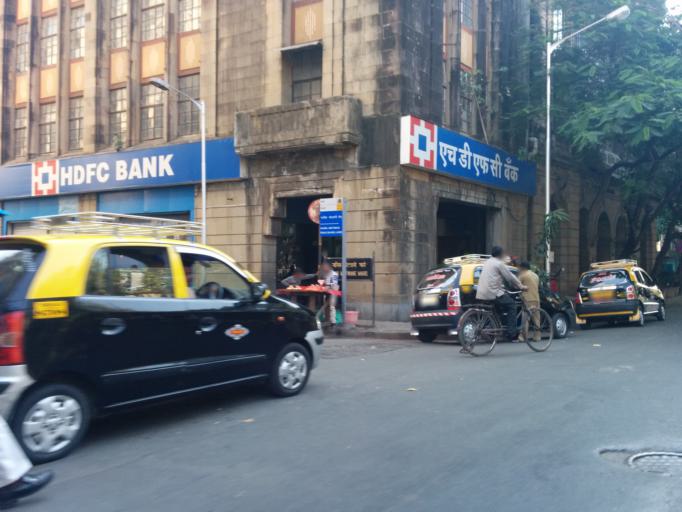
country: IN
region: Maharashtra
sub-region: Raigarh
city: Uran
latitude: 18.9291
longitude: 72.8314
